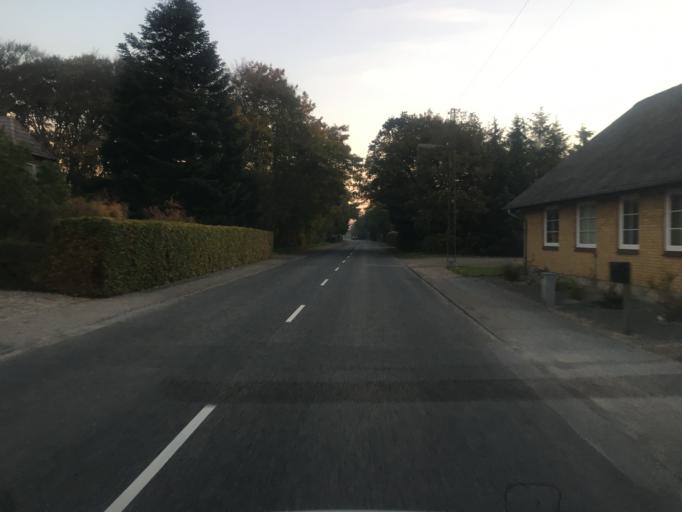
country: DE
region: Schleswig-Holstein
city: Bramstedtlund
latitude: 54.9525
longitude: 9.1053
